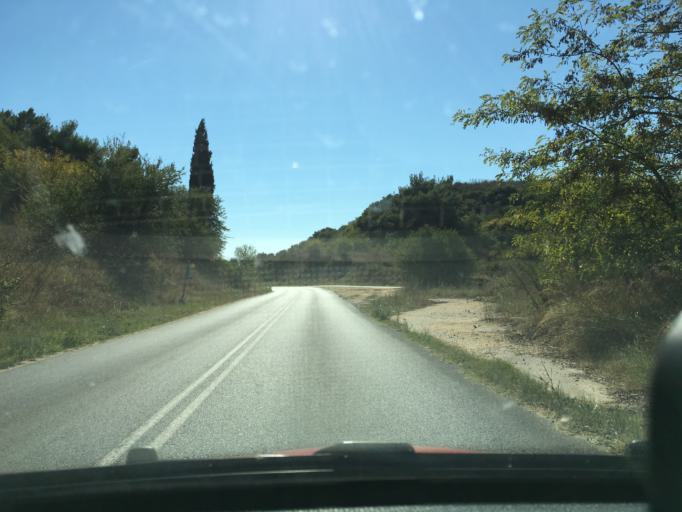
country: GR
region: Central Macedonia
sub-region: Nomos Chalkidikis
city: Nea Roda
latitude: 40.3670
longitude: 23.9177
